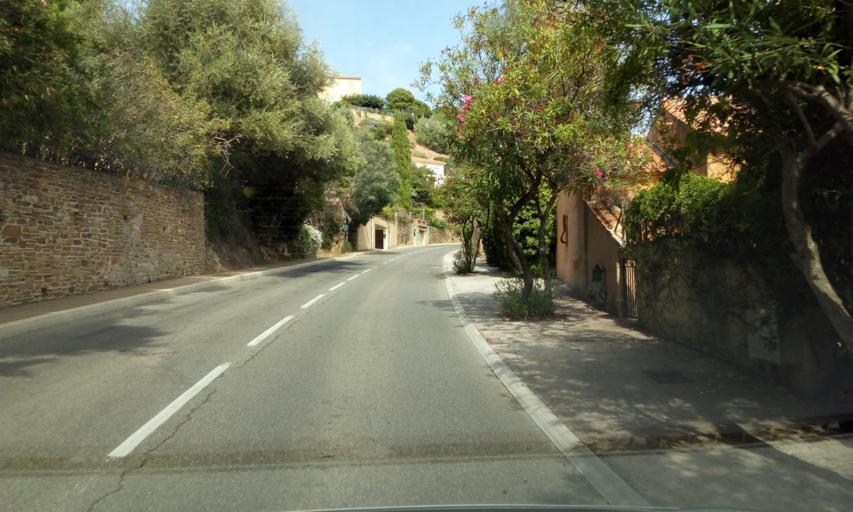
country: FR
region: Provence-Alpes-Cote d'Azur
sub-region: Departement du Var
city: Bormes-les-Mimosas
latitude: 43.1477
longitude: 6.3412
